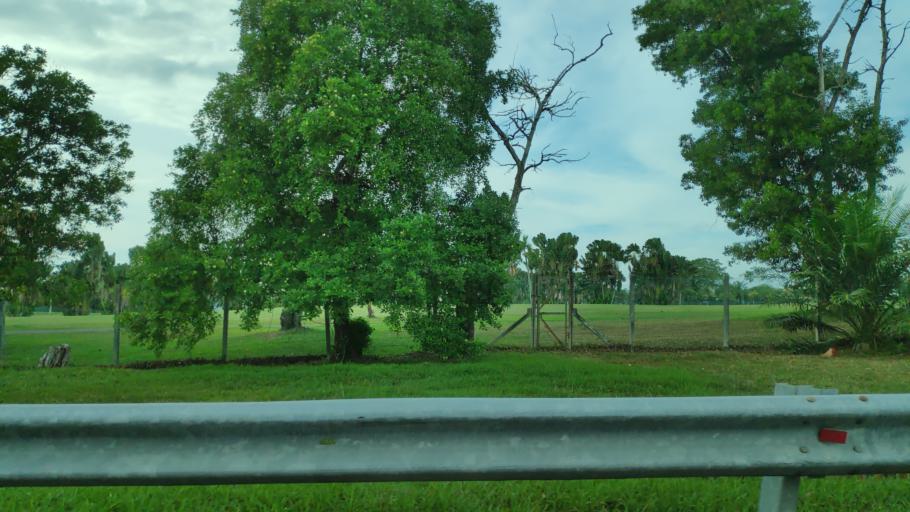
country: BN
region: Brunei and Muara
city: Bandar Seri Begawan
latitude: 4.9375
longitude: 114.9336
